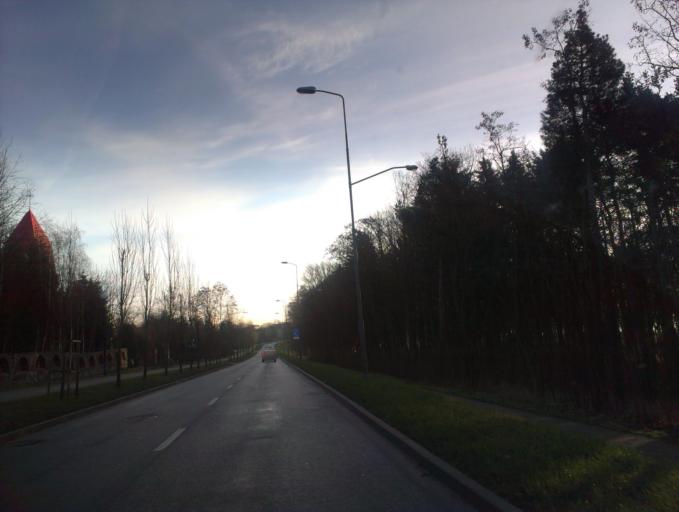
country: PL
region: West Pomeranian Voivodeship
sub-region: Powiat szczecinecki
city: Szczecinek
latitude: 53.7164
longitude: 16.6601
